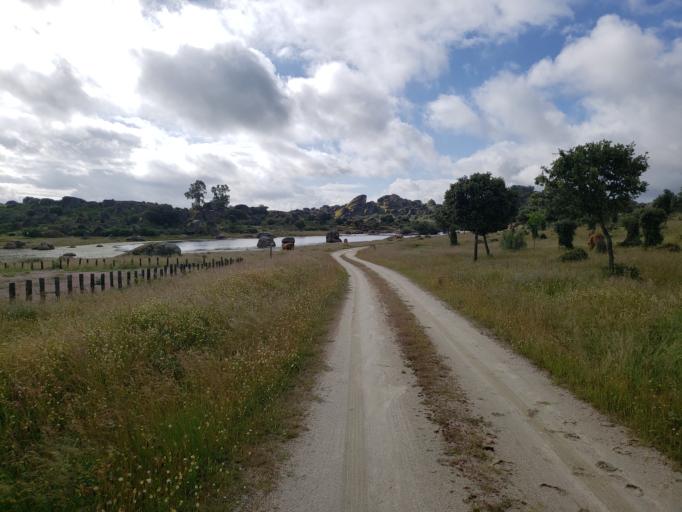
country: ES
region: Extremadura
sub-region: Provincia de Caceres
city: Malpartida de Caceres
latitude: 39.4264
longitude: -6.5000
